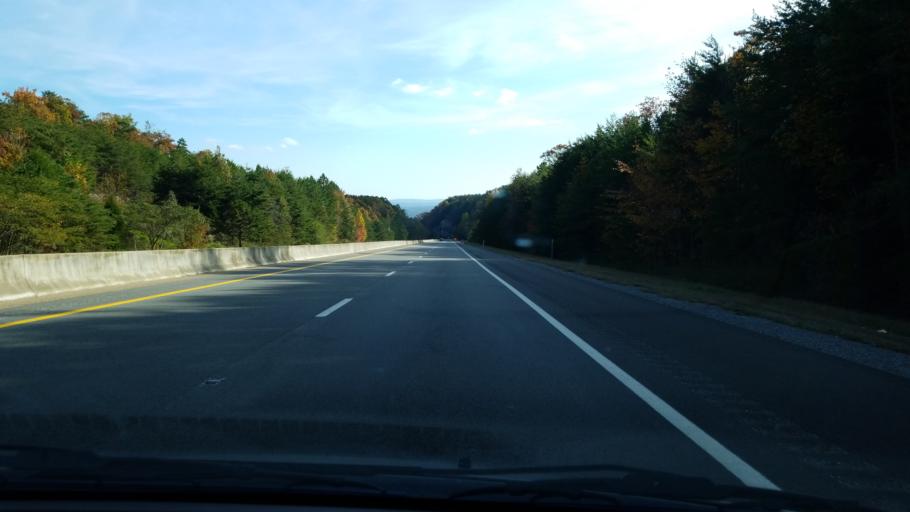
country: US
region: Tennessee
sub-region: Hamilton County
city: Sale Creek
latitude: 35.3340
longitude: -85.1656
